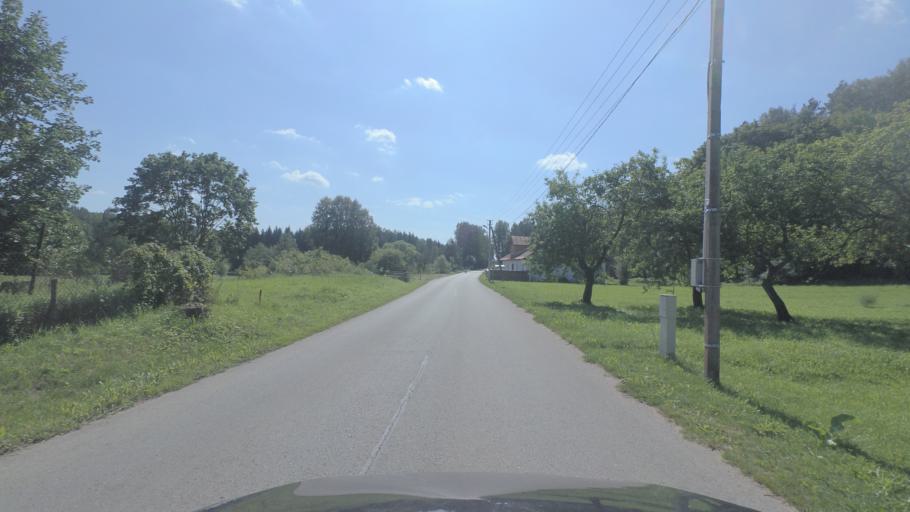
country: LT
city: Nemencine
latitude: 54.8464
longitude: 25.3733
